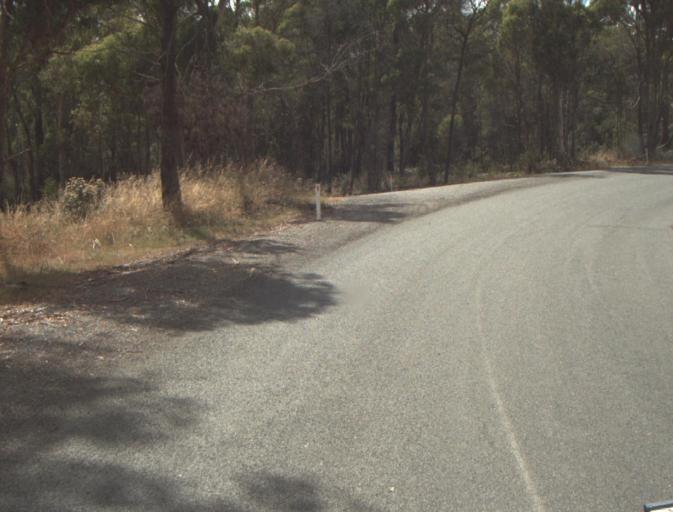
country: AU
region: Tasmania
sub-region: Launceston
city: Mayfield
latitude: -41.2086
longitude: 147.1293
